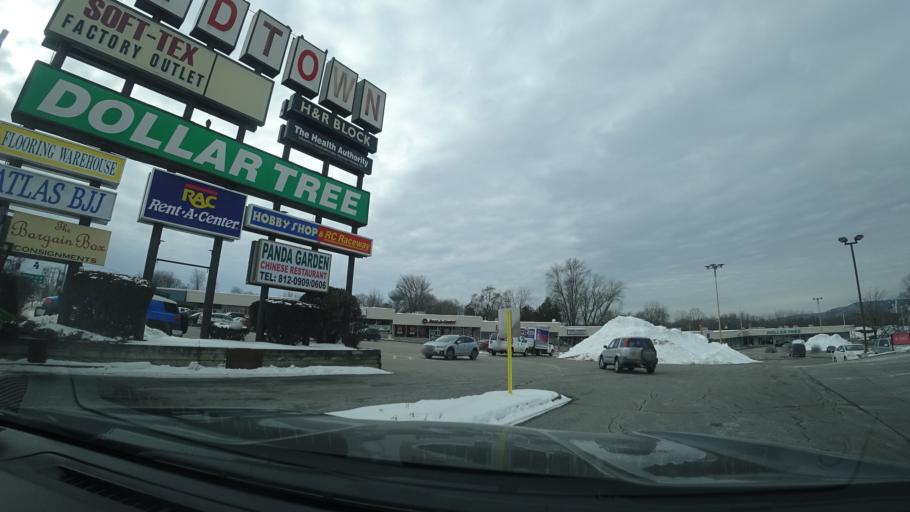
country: US
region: New York
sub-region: Saratoga County
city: South Glens Falls
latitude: 43.2999
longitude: -73.6361
